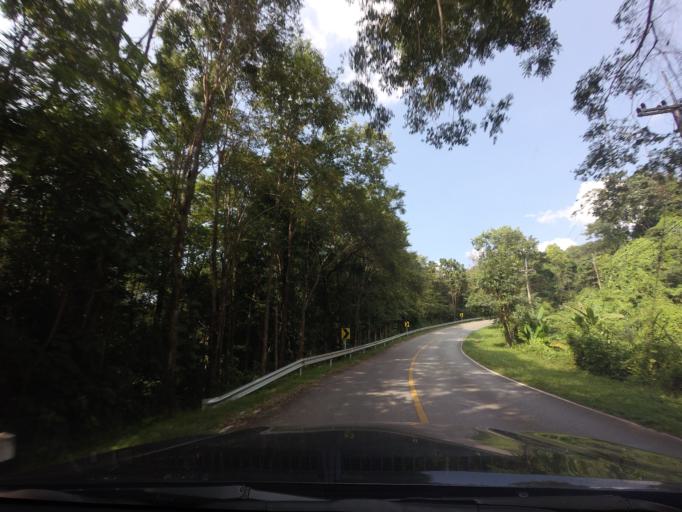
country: TH
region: Phitsanulok
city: Nakhon Thai
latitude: 17.0197
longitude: 100.9568
